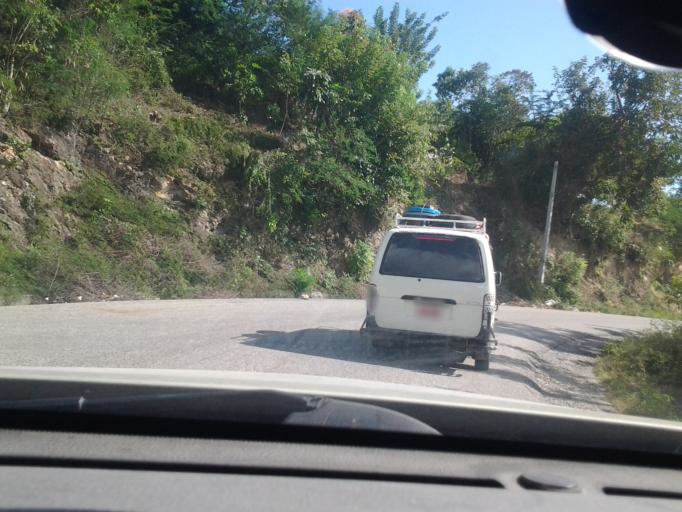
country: HT
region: Sud-Est
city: Jacmel
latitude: 18.2806
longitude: -72.5703
